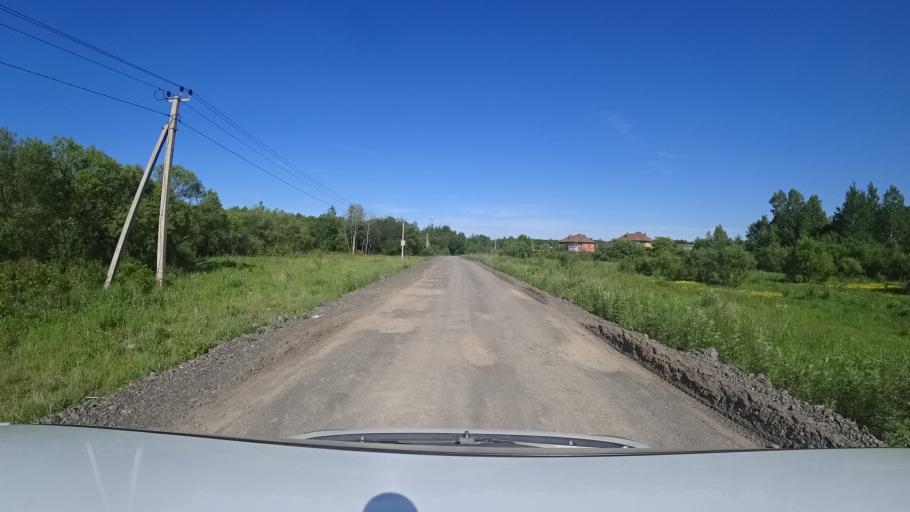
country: RU
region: Khabarovsk Krai
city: Topolevo
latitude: 48.5528
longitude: 135.1835
